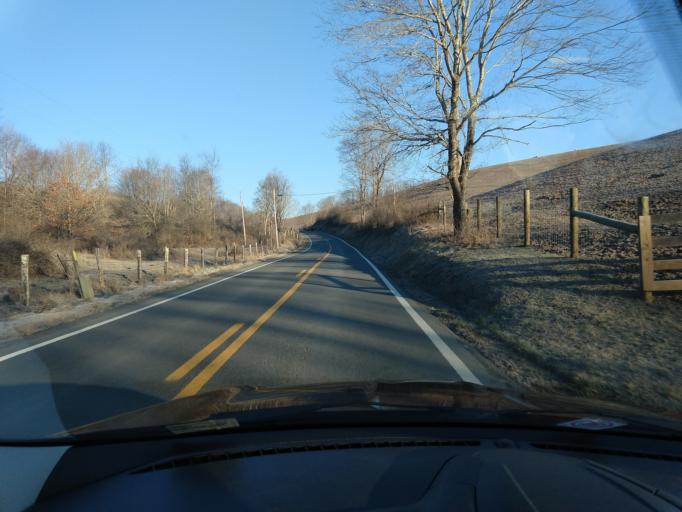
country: US
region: West Virginia
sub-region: Greenbrier County
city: Rainelle
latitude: 37.8678
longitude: -80.7235
